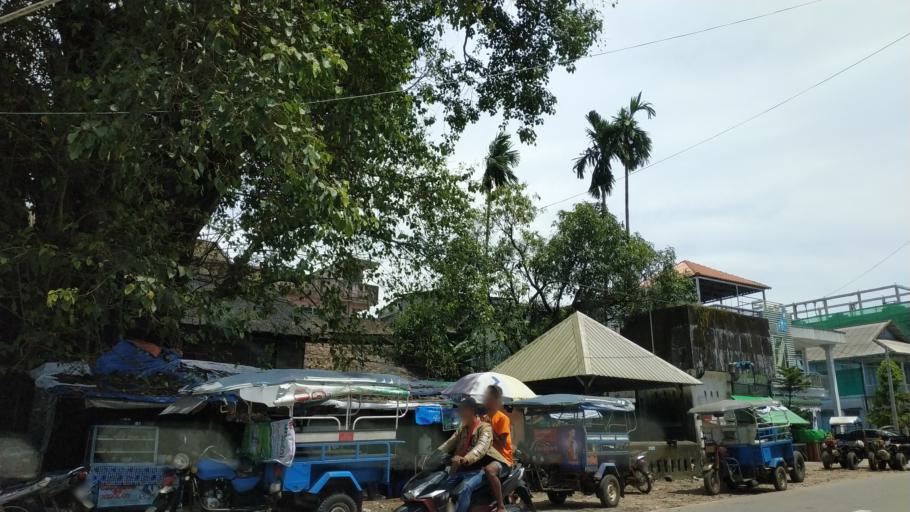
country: MM
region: Tanintharyi
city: Dawei
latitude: 14.0691
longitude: 98.1900
